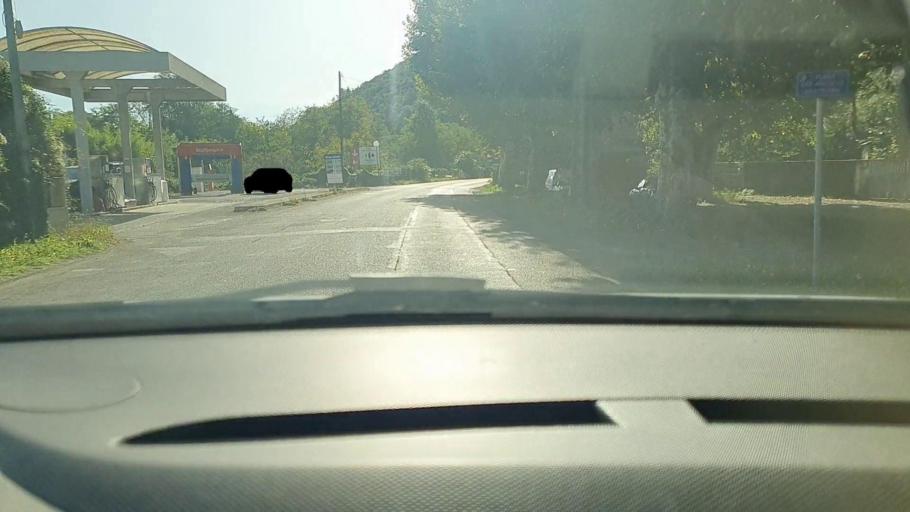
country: FR
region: Languedoc-Roussillon
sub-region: Departement du Gard
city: Besseges
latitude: 44.2860
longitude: 4.1071
